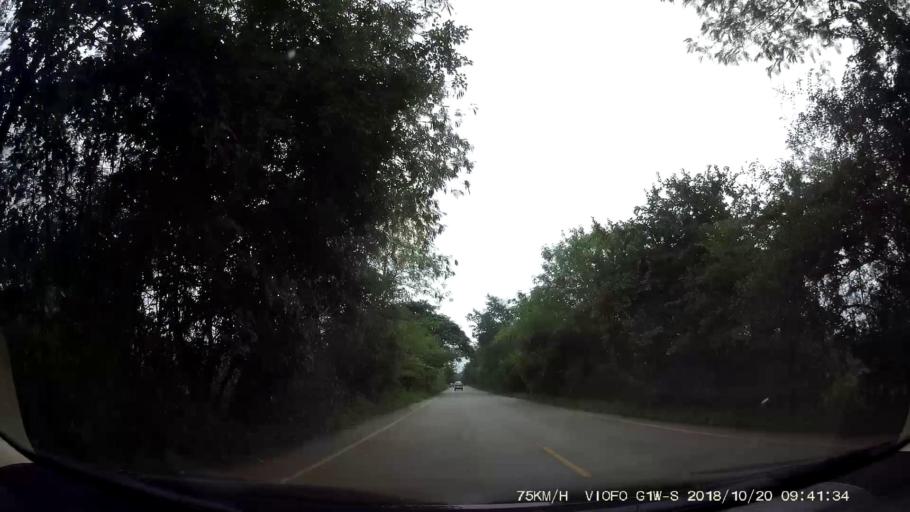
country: TH
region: Chaiyaphum
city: Khon San
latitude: 16.4547
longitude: 101.9564
